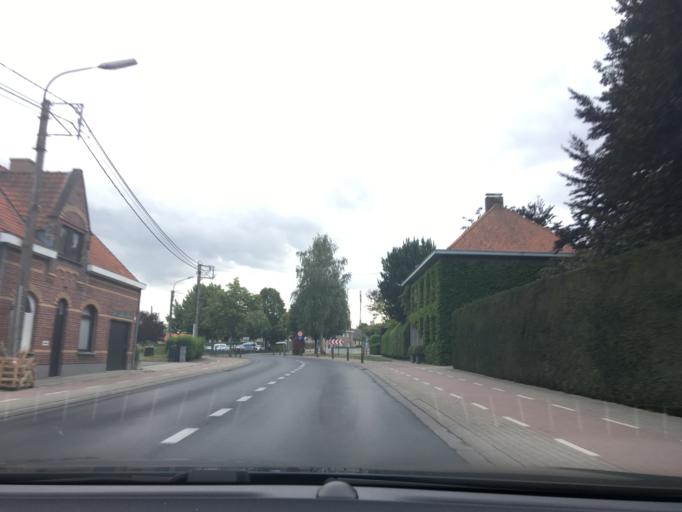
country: BE
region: Flanders
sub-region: Provincie West-Vlaanderen
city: Staden
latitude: 50.9343
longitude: 3.0166
